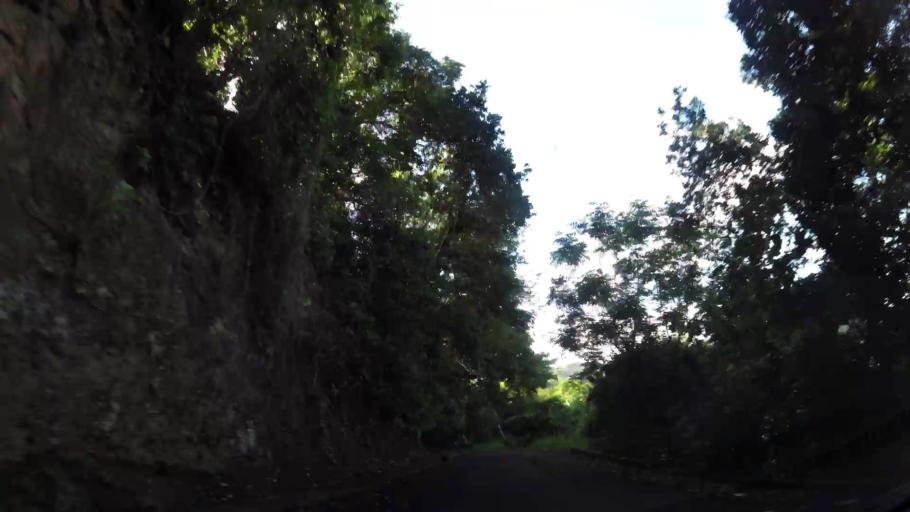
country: DM
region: Saint Andrew
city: Calibishie
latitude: 15.5935
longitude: -61.3775
